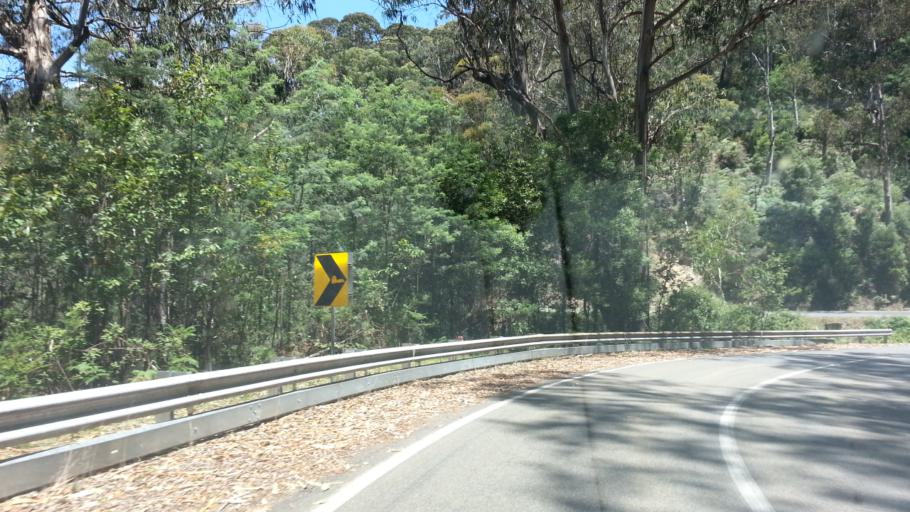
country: AU
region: Victoria
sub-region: Alpine
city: Mount Beauty
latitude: -36.7730
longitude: 147.2142
